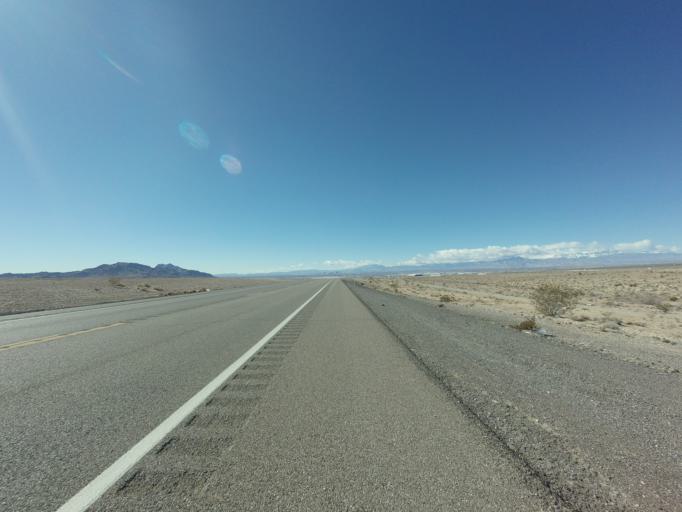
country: US
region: Nevada
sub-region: Clark County
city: Nellis Air Force Base
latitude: 36.2978
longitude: -114.9614
